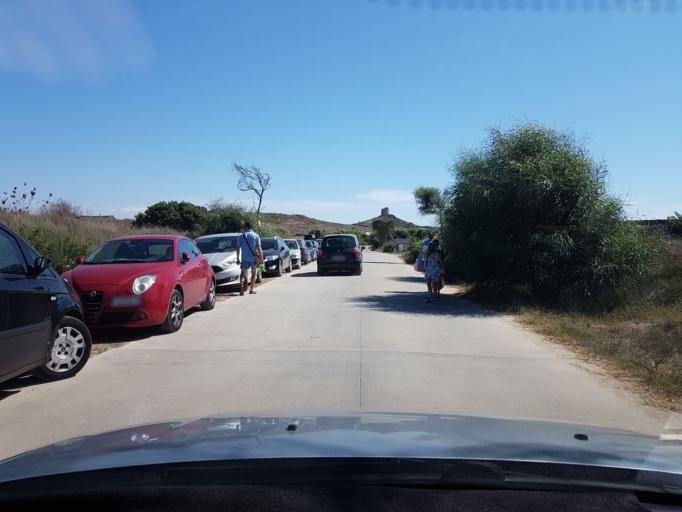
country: IT
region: Sardinia
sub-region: Provincia di Oristano
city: Cabras
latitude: 39.8817
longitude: 8.4392
